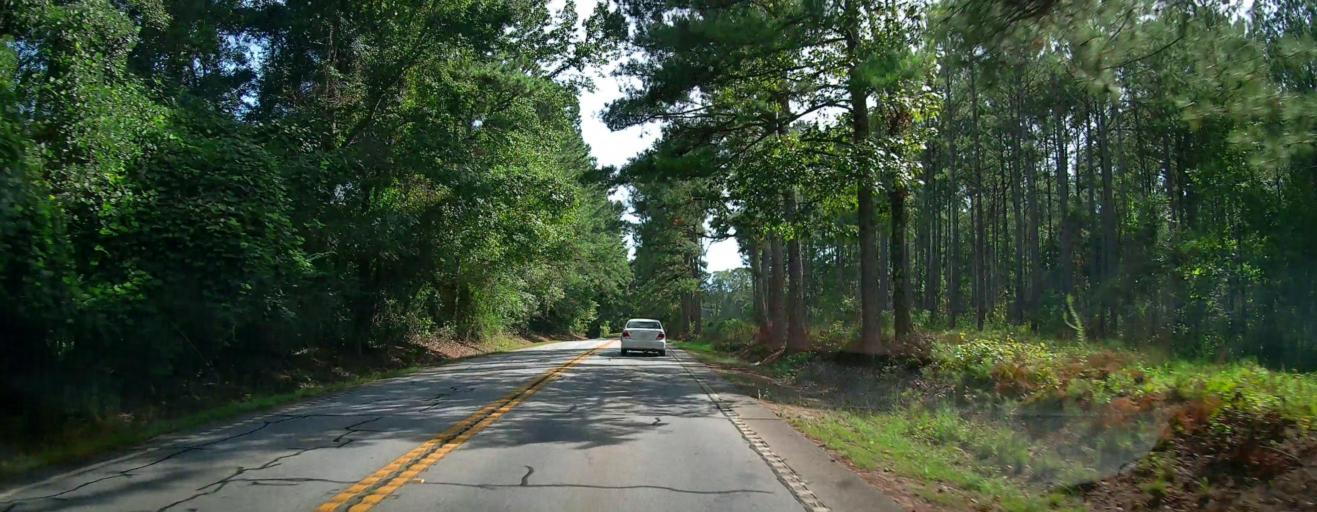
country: US
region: Georgia
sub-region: Harris County
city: Hamilton
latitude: 32.6828
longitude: -84.8579
